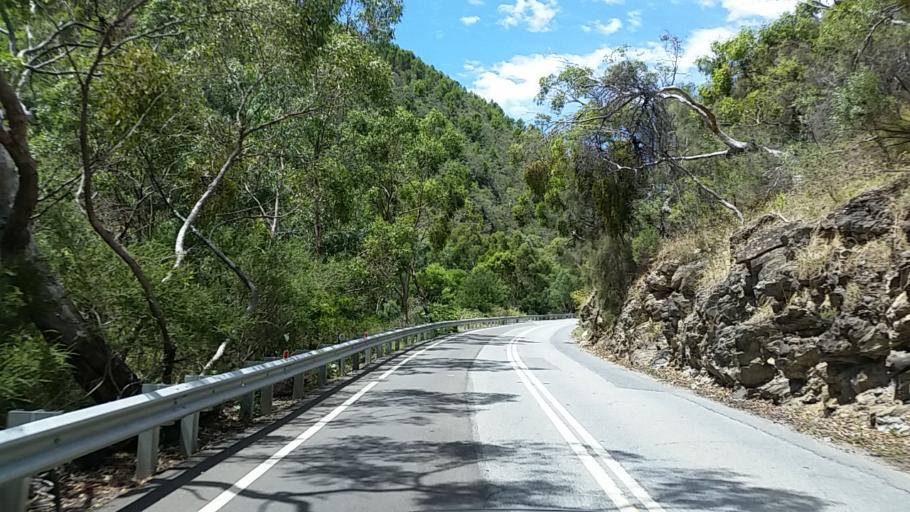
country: AU
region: South Australia
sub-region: Campbelltown
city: Athelstone
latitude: -34.8594
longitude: 138.7348
